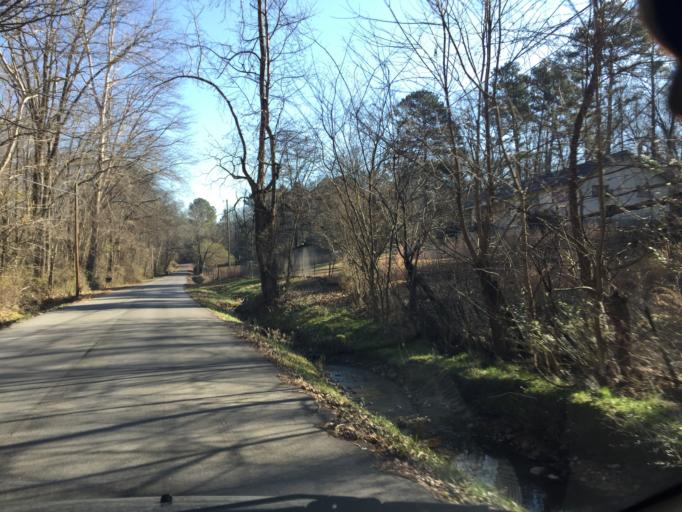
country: US
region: Tennessee
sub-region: Hamilton County
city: Collegedale
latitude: 35.0803
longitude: -85.0812
